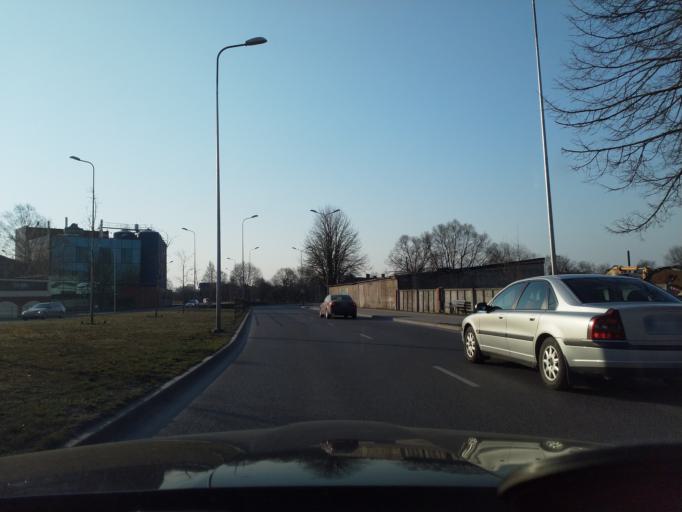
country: LV
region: Liepaja
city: Liepaja
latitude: 56.5112
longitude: 21.0224
